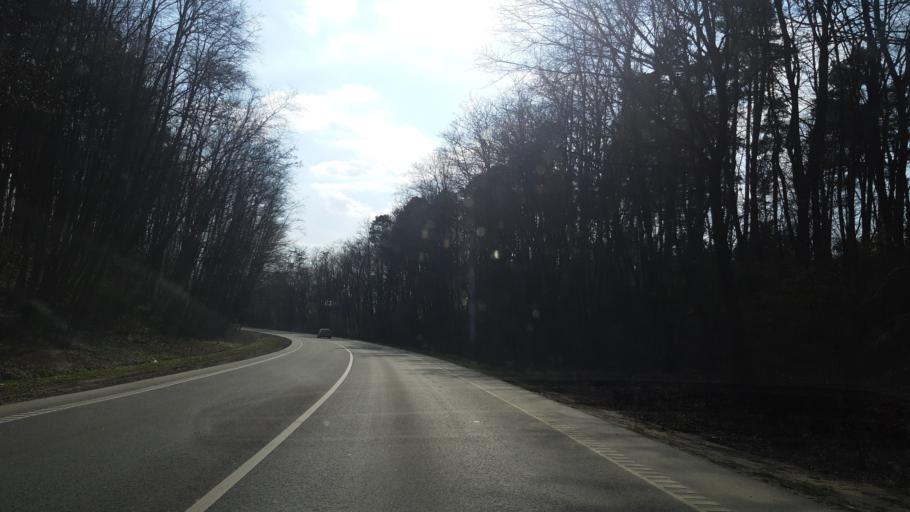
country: LT
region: Kauno apskritis
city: Dainava (Kaunas)
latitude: 54.8707
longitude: 23.9899
